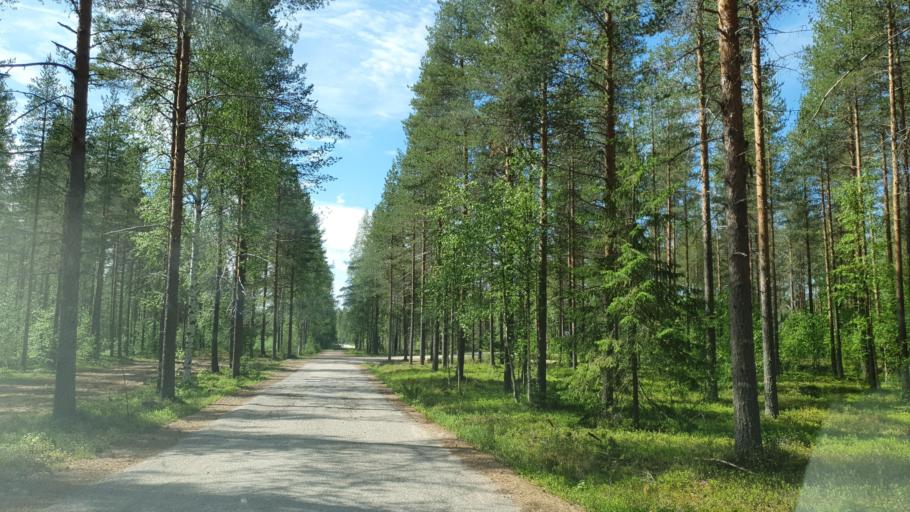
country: FI
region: Kainuu
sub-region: Kehys-Kainuu
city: Hyrynsalmi
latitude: 64.6943
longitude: 28.4874
